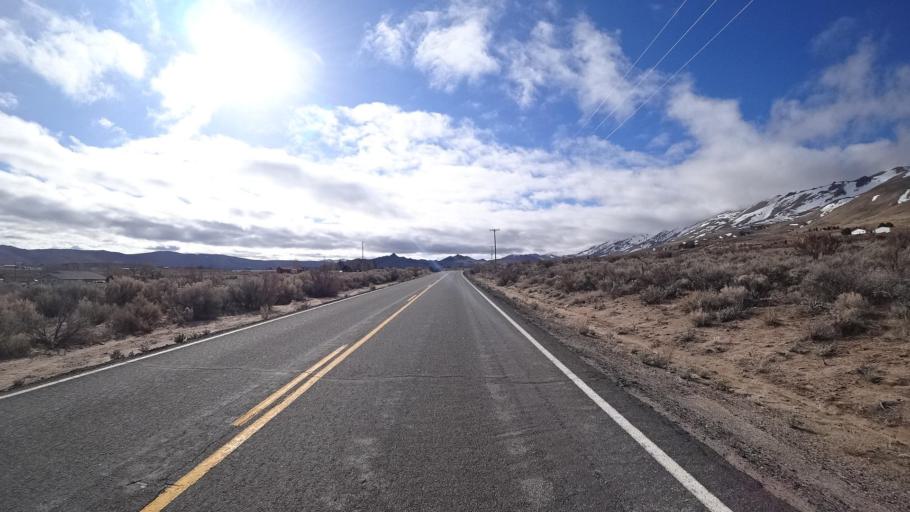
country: US
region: Nevada
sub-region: Washoe County
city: Cold Springs
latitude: 39.8750
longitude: -119.9641
